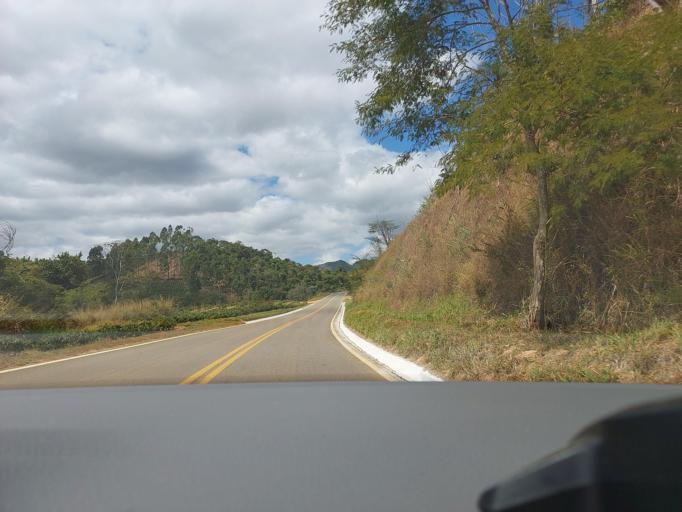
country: BR
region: Minas Gerais
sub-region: Visconde Do Rio Branco
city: Visconde do Rio Branco
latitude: -20.9367
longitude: -42.6291
